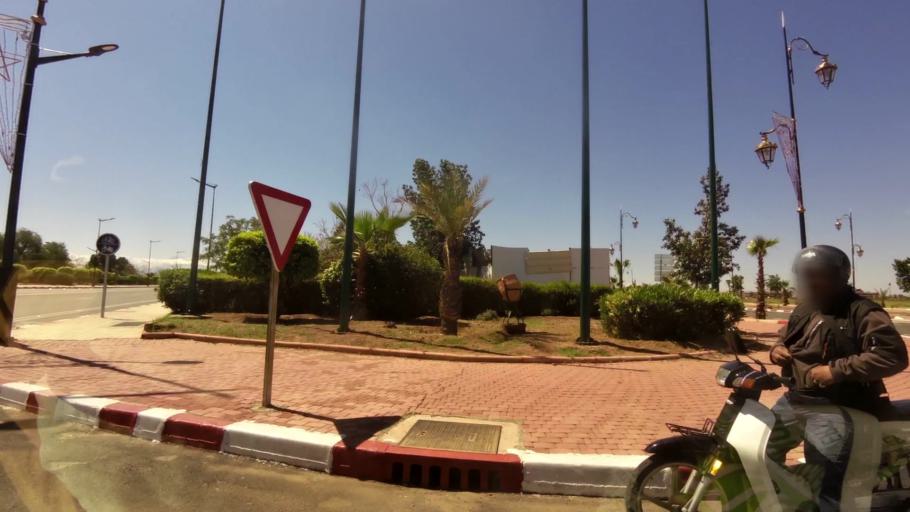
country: MA
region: Marrakech-Tensift-Al Haouz
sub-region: Marrakech
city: Marrakesh
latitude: 31.6043
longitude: -7.9885
